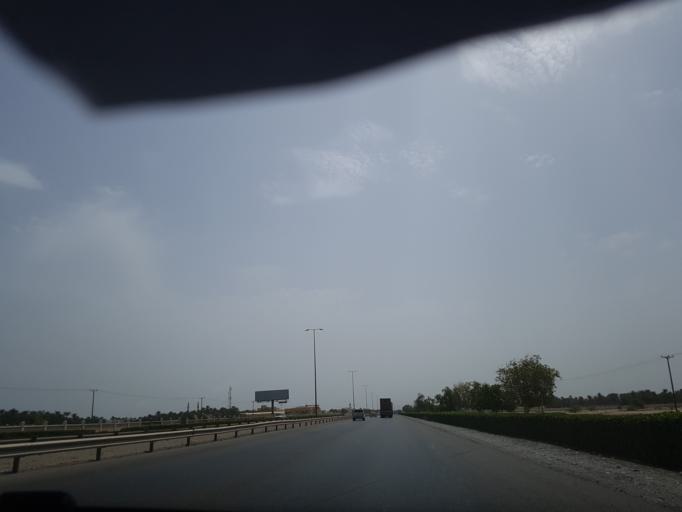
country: OM
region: Al Batinah
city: Barka'
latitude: 23.7357
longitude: 57.6698
